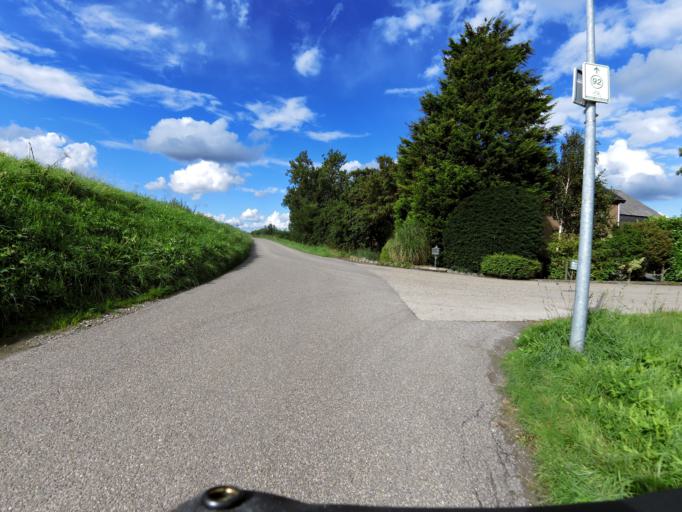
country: NL
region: South Holland
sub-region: Gemeente Goeree-Overflakkee
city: Middelharnis
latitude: 51.6859
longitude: 4.2127
